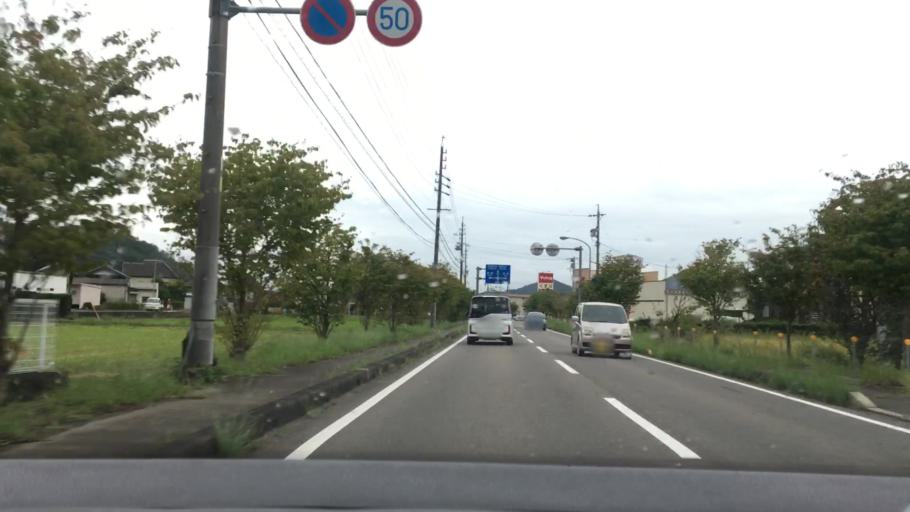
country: JP
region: Gifu
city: Mino
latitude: 35.5225
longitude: 136.8525
